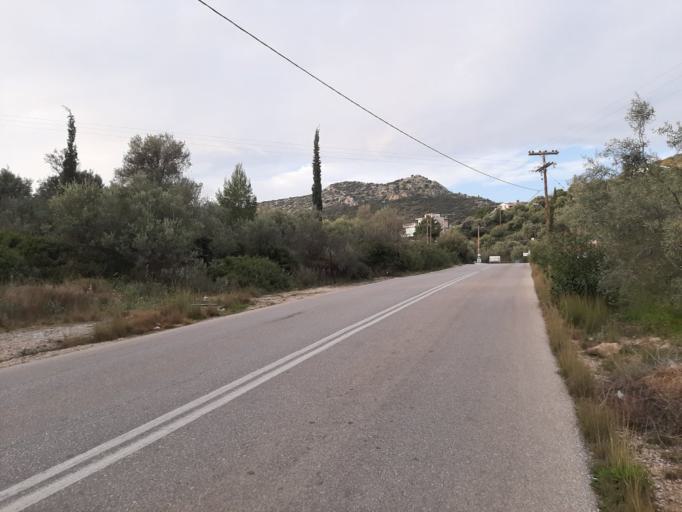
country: GR
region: Peloponnese
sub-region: Nomos Argolidos
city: Tolon
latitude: 37.5242
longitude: 22.8583
